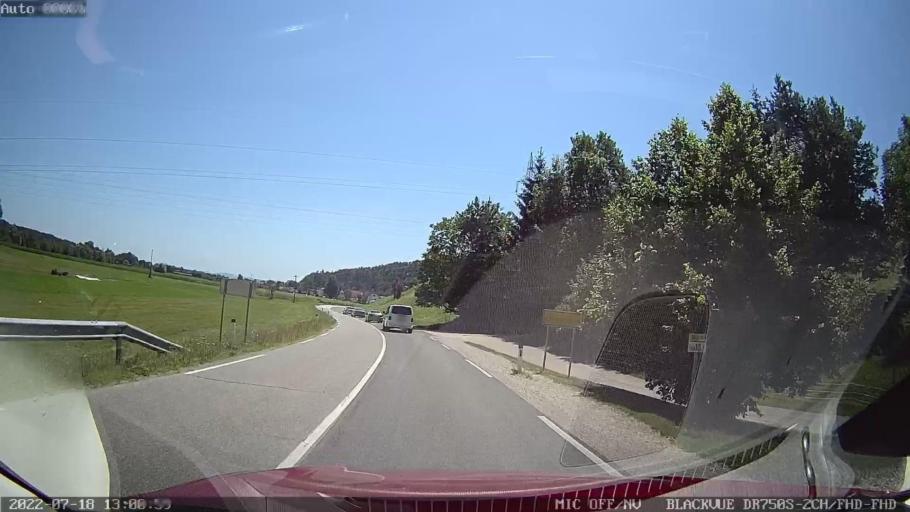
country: SI
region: Dobrova-Horjul-Polhov Gradec
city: Dobrova
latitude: 46.0582
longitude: 14.4140
